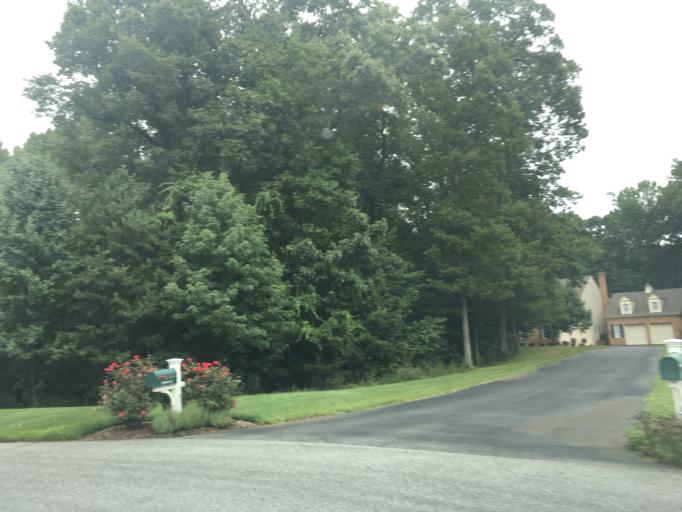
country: US
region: Maryland
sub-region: Anne Arundel County
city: Crownsville
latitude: 39.0330
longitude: -76.5982
